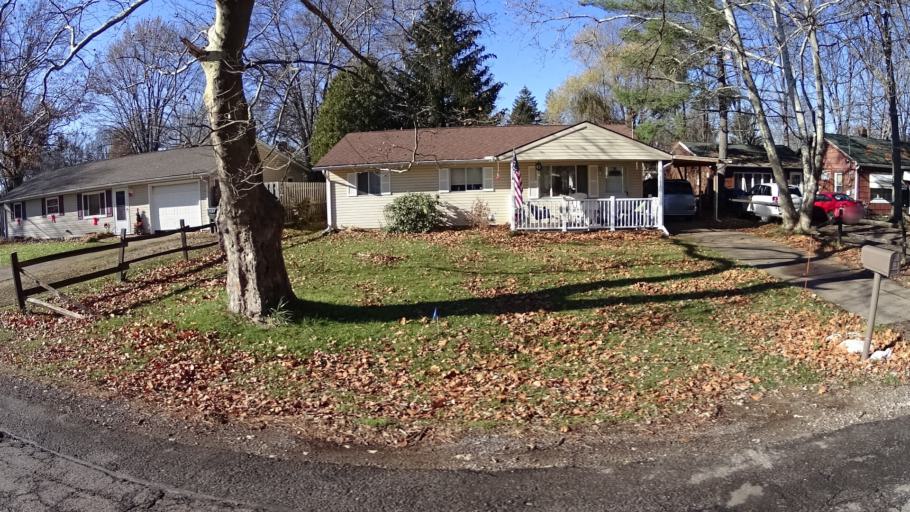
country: US
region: Ohio
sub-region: Lorain County
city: North Ridgeville
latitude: 41.3996
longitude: -81.9975
